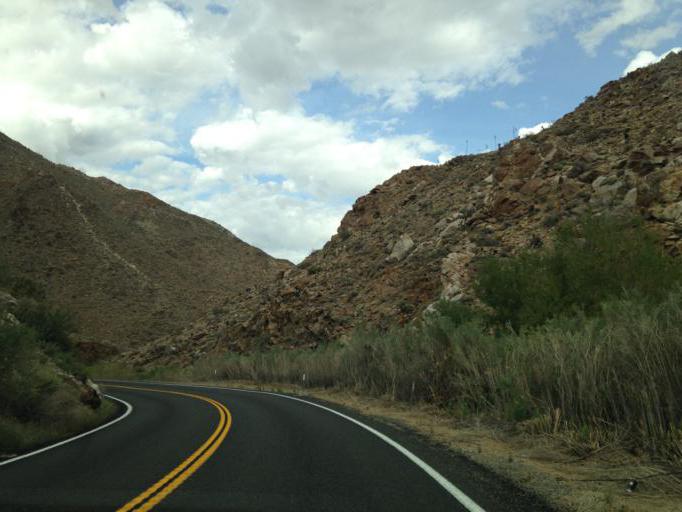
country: US
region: California
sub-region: San Diego County
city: Julian
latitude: 33.1088
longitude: -116.4492
